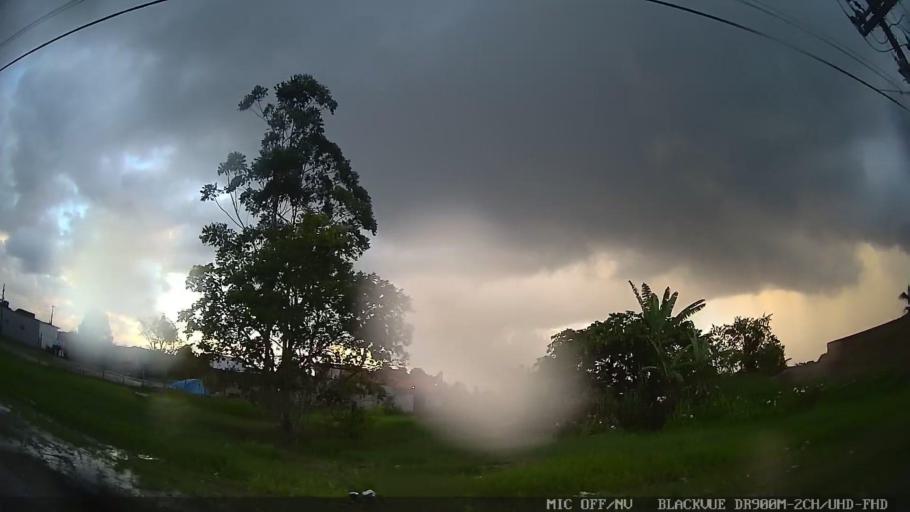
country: BR
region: Sao Paulo
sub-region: Itanhaem
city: Itanhaem
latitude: -24.1516
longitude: -46.7793
